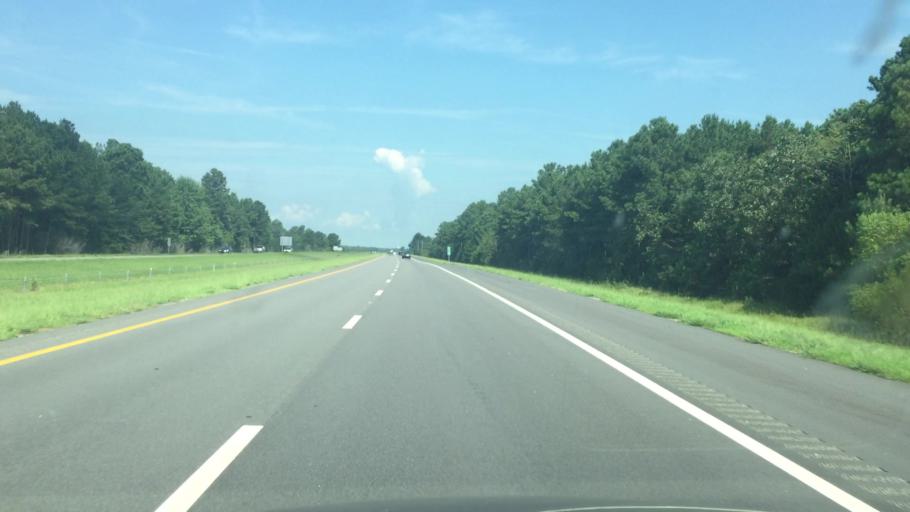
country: US
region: North Carolina
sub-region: Robeson County
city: Maxton
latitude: 34.6933
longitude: -79.2847
